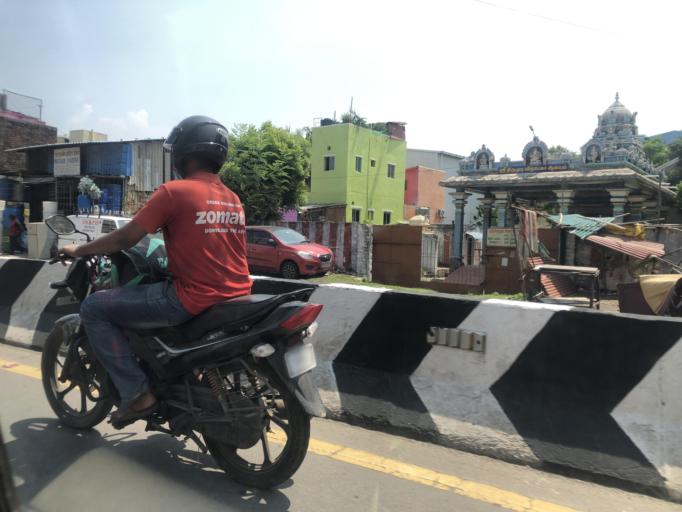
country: IN
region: Tamil Nadu
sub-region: Chennai
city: Gandhi Nagar
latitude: 12.9817
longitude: 80.2594
